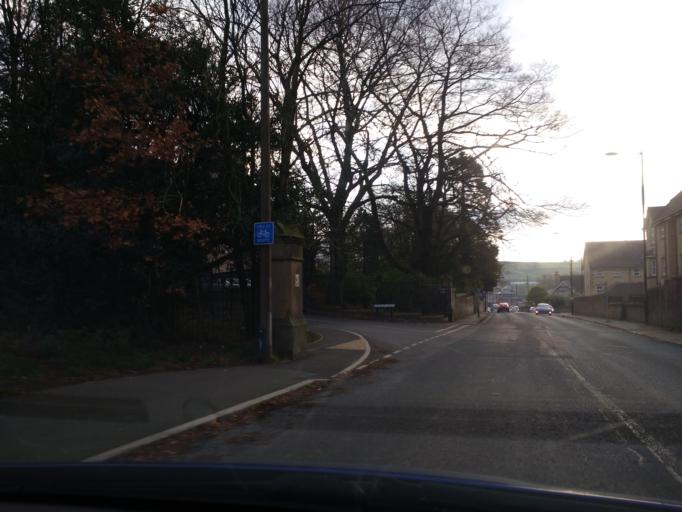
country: GB
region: England
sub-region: Lancashire
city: Lancaster
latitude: 54.0486
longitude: -2.7748
